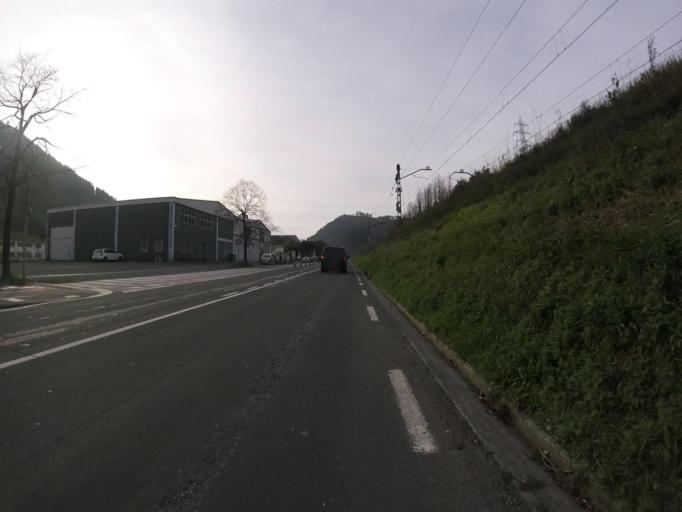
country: ES
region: Basque Country
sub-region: Provincia de Guipuzcoa
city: Anoeta
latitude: 43.1562
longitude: -2.0688
